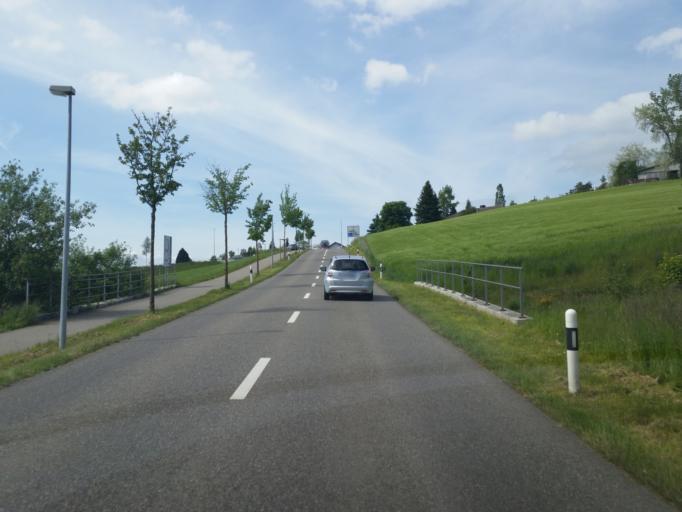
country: CH
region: Aargau
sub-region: Bezirk Bremgarten
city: Berikon
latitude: 47.3415
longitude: 8.3818
